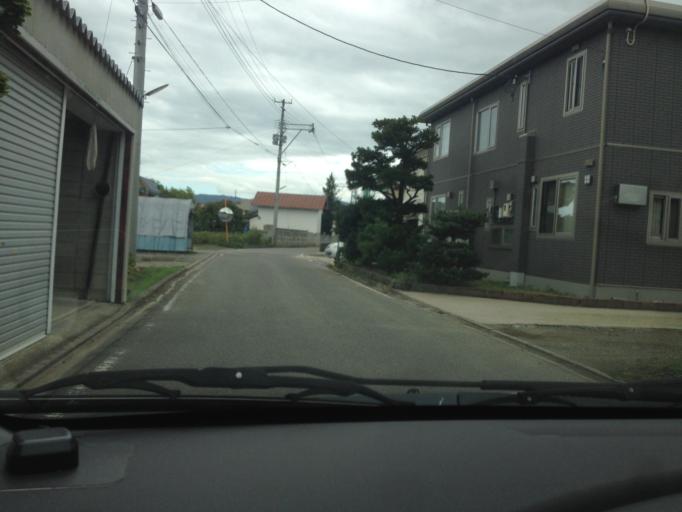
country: JP
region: Fukushima
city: Kitakata
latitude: 37.4727
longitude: 139.8543
